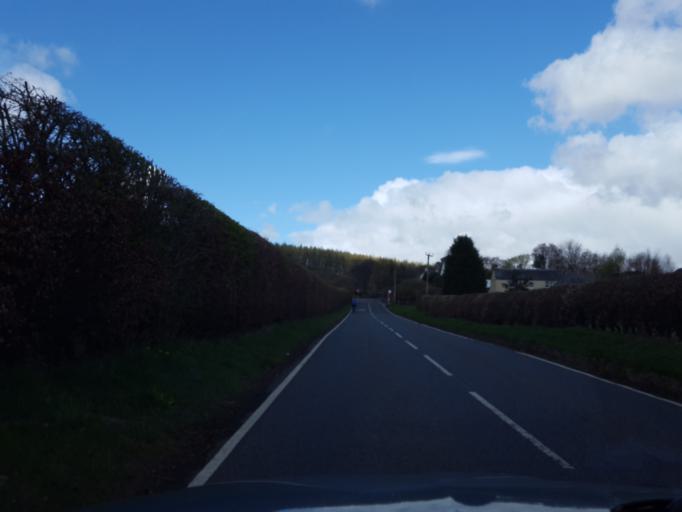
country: GB
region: Scotland
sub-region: Clackmannanshire
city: Dollar
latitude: 56.1940
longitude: -3.6037
